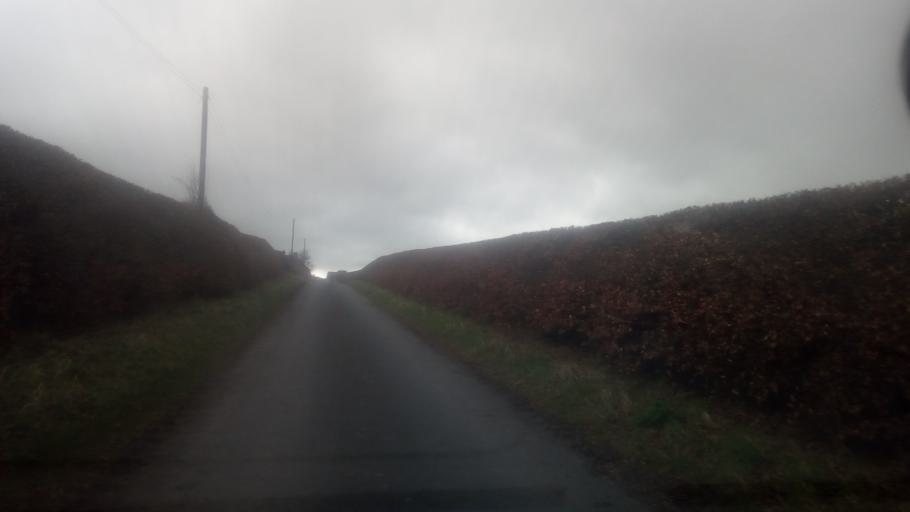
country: GB
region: Scotland
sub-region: The Scottish Borders
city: Jedburgh
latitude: 55.5050
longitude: -2.5027
